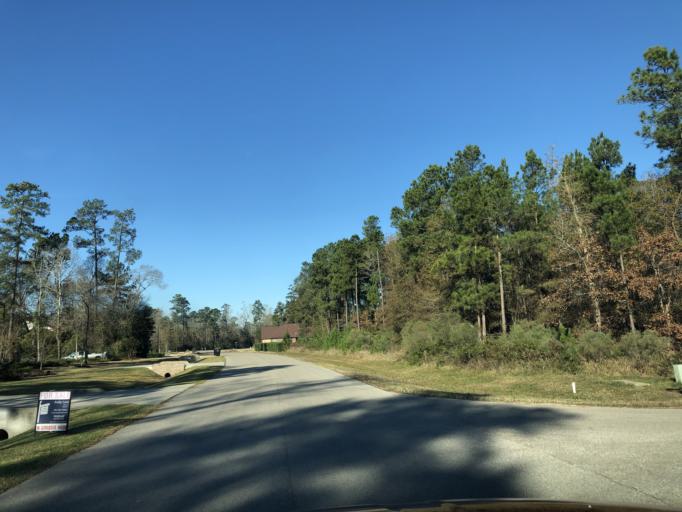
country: US
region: Texas
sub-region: Montgomery County
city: Porter Heights
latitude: 30.0683
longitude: -95.3254
